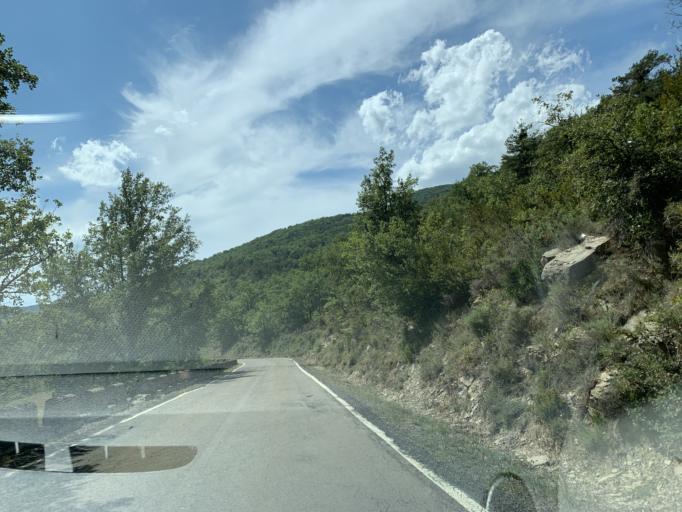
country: ES
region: Aragon
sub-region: Provincia de Huesca
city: Jasa
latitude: 42.6285
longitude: -0.6507
